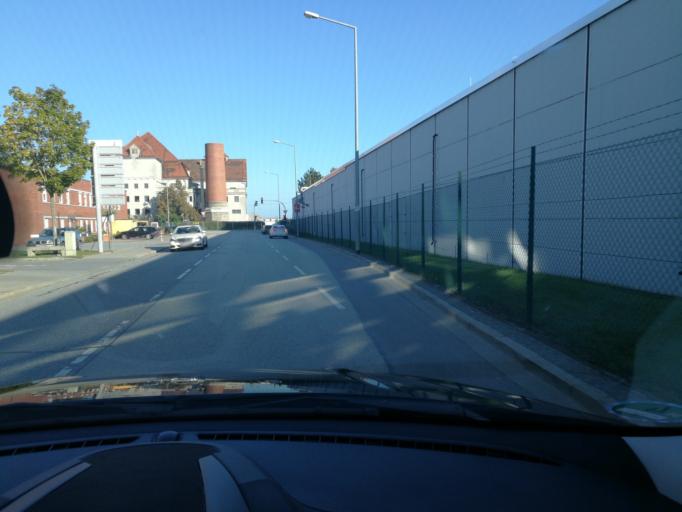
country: DE
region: Bavaria
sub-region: Upper Palatinate
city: Regensburg
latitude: 49.0101
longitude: 12.1442
